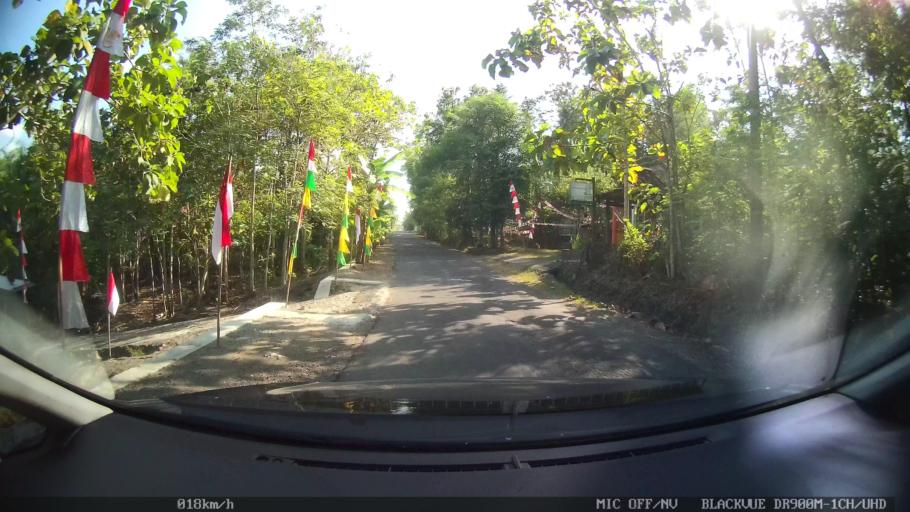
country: ID
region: Daerah Istimewa Yogyakarta
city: Kasihan
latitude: -7.8337
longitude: 110.2871
